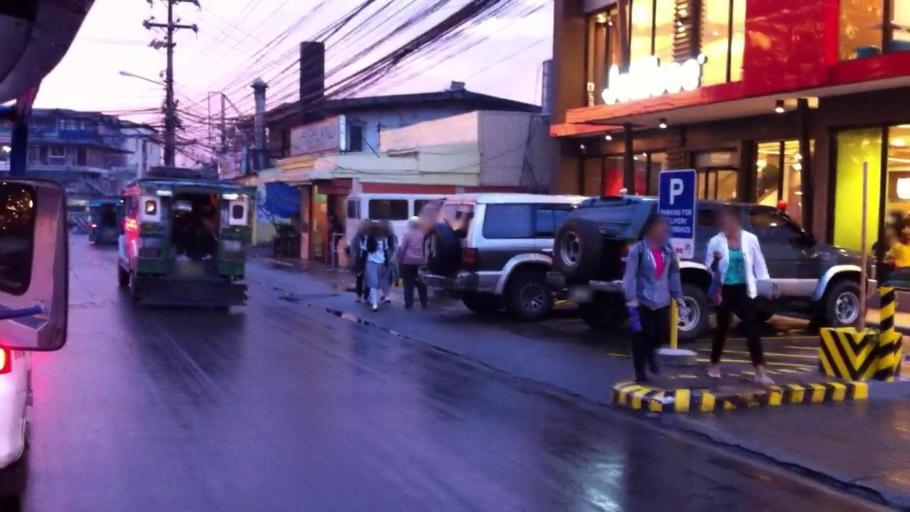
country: PH
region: Cordillera
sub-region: Province of Benguet
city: La Trinidad
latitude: 16.4473
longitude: 120.5908
